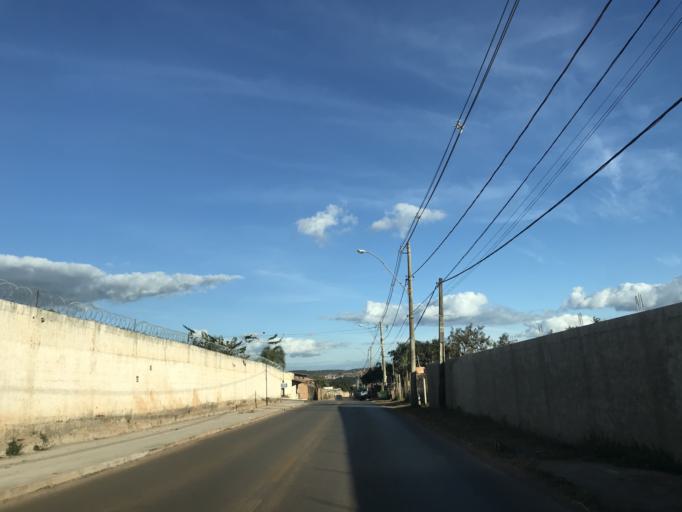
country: BR
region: Federal District
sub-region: Brasilia
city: Brasilia
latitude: -15.8839
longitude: -47.7667
